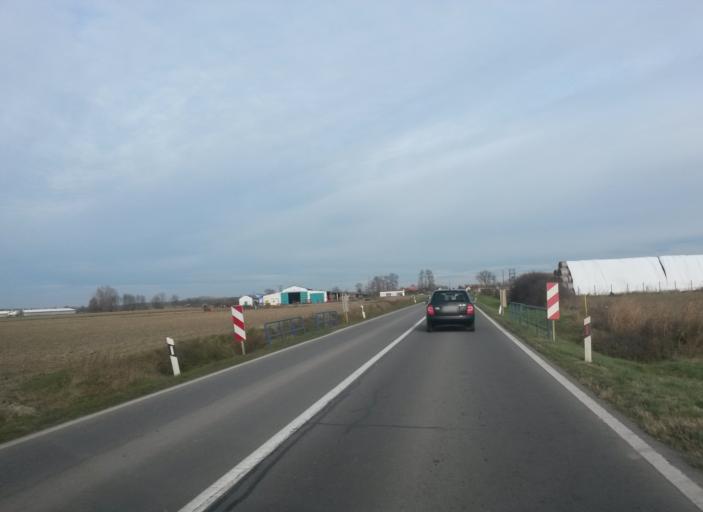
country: HR
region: Osjecko-Baranjska
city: Viskovci
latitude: 45.3970
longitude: 18.4588
